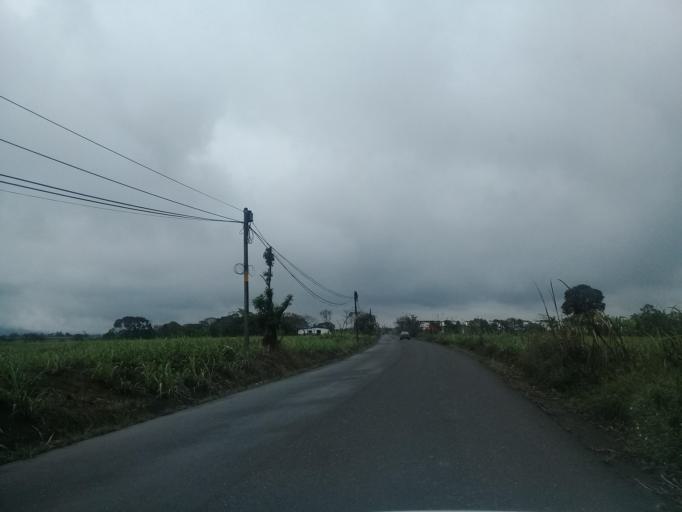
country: MX
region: Veracruz
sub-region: Amatlan de los Reyes
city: Trapiche Viejo
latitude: 18.8316
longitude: -96.9559
